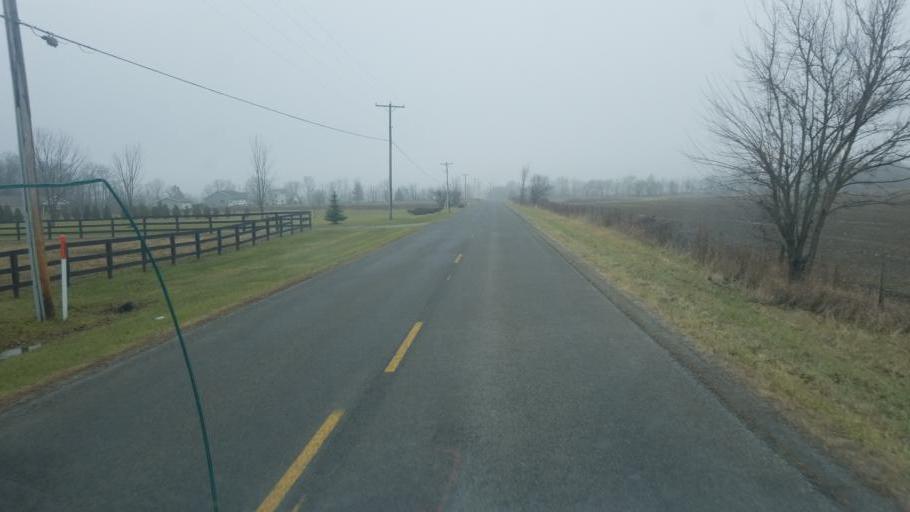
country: US
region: Ohio
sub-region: Champaign County
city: North Lewisburg
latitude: 40.3562
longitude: -83.5534
